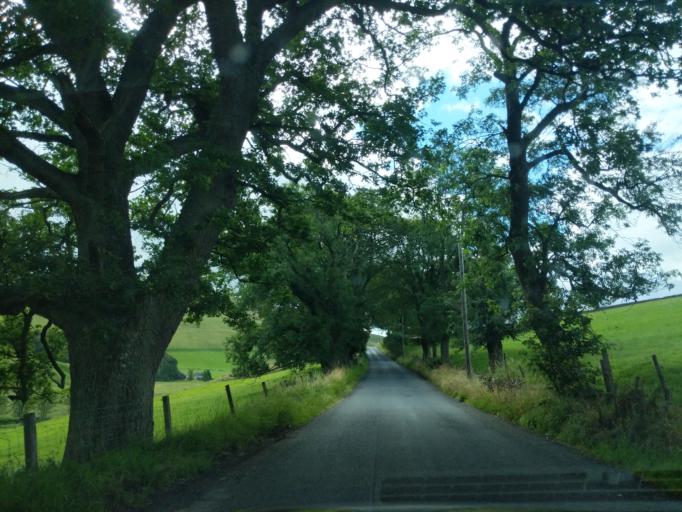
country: GB
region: Scotland
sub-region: The Scottish Borders
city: West Linton
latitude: 55.6954
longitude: -3.3357
